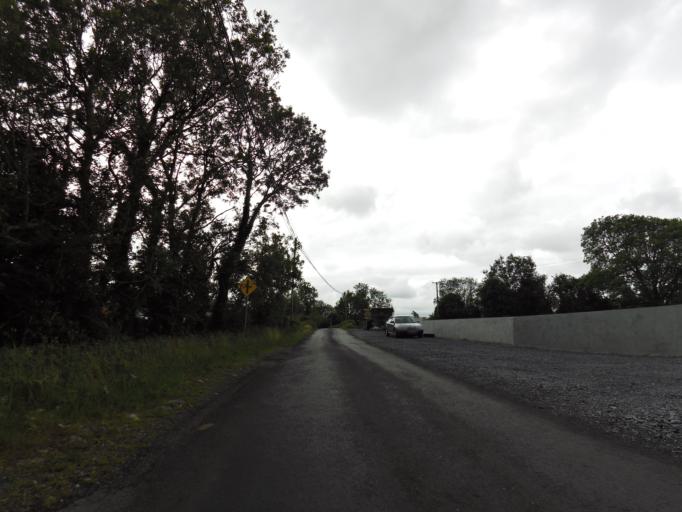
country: IE
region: Connaught
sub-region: County Galway
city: Athenry
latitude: 53.2957
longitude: -8.7101
